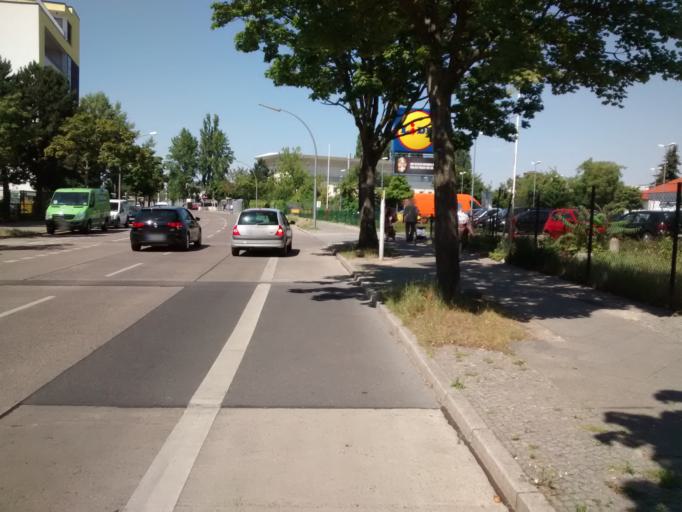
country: DE
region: Berlin
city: Charlottenburg-Nord
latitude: 52.5274
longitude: 13.3065
